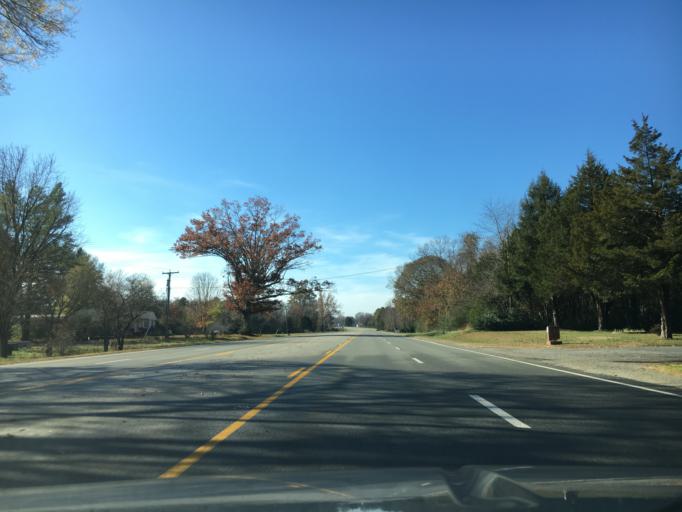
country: US
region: Virginia
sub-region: Cumberland County
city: Cumberland
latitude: 37.4860
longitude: -78.2651
